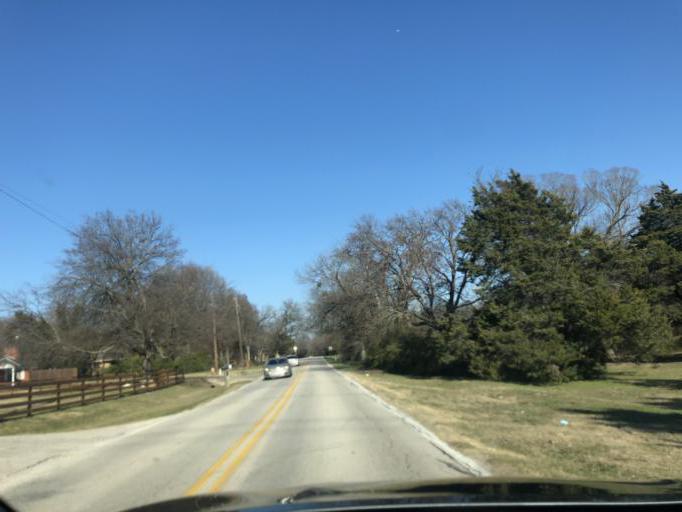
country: US
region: Texas
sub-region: Dallas County
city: Duncanville
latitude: 32.6202
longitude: -96.9303
